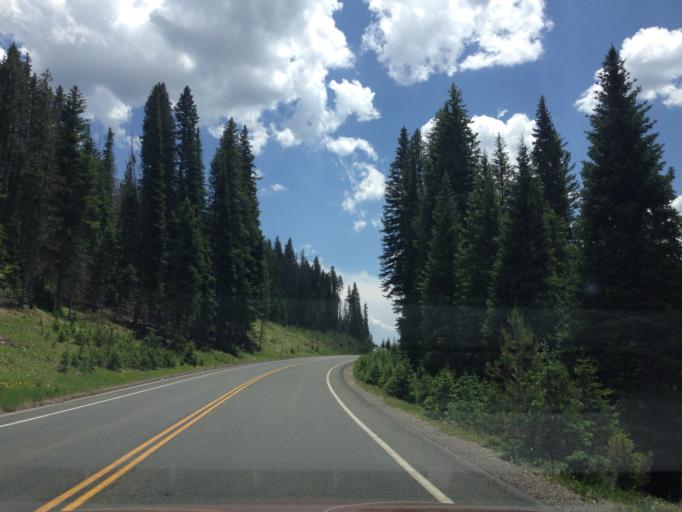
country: US
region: Colorado
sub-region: Grand County
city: Granby
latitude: 40.3484
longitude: -105.8574
